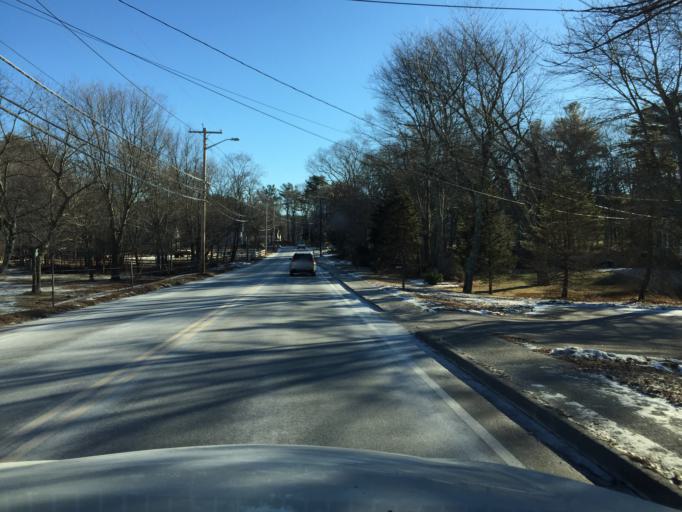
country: US
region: Massachusetts
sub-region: Bristol County
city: Mansfield
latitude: 42.0629
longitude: -71.2168
